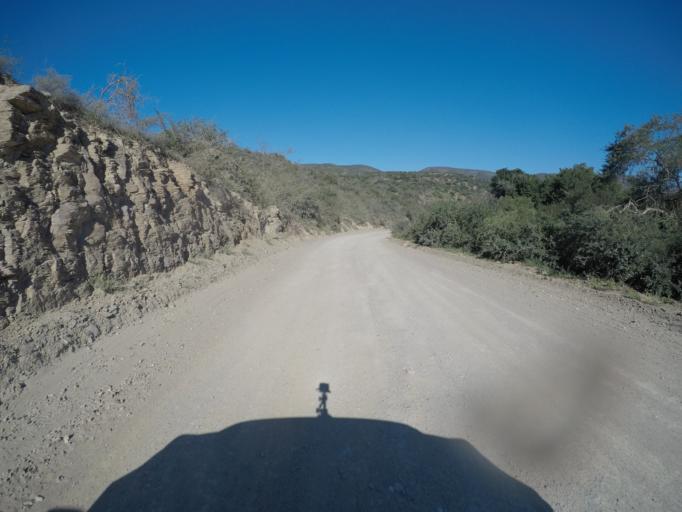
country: ZA
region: Eastern Cape
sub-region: Cacadu District Municipality
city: Kruisfontein
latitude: -33.6701
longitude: 24.5761
